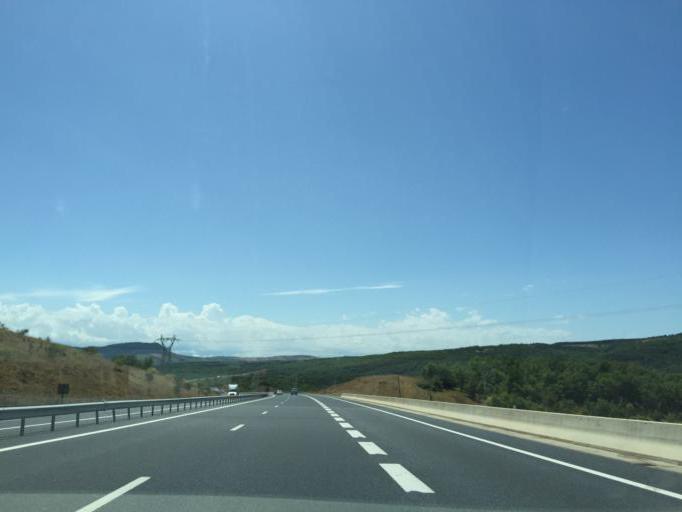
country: FR
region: Midi-Pyrenees
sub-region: Departement de l'Aveyron
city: Millau
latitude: 44.2114
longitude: 3.0692
